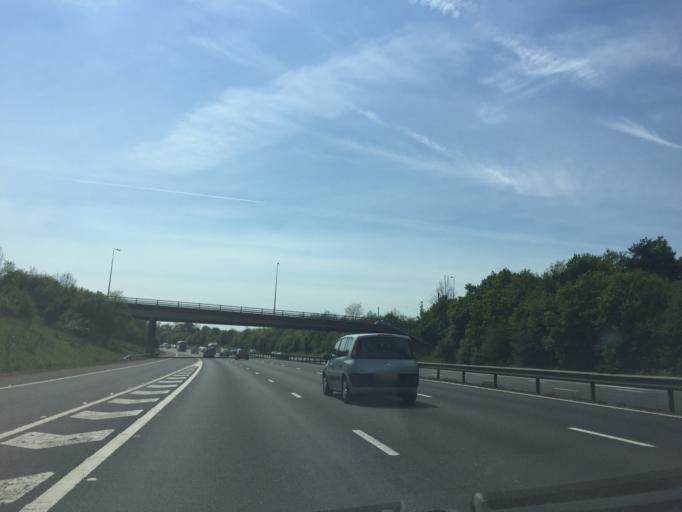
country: GB
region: England
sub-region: Essex
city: Chigwell
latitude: 51.6269
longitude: 0.0660
